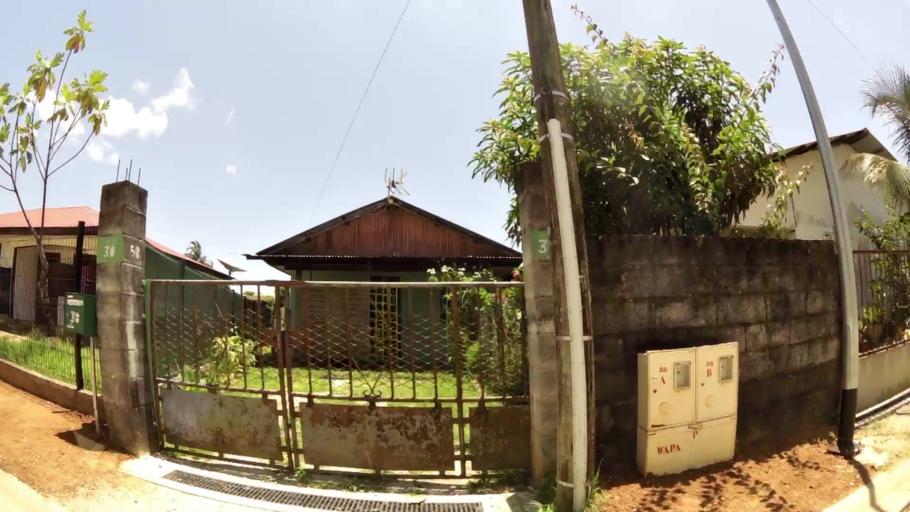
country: GF
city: Macouria
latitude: 4.8863
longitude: -52.3413
